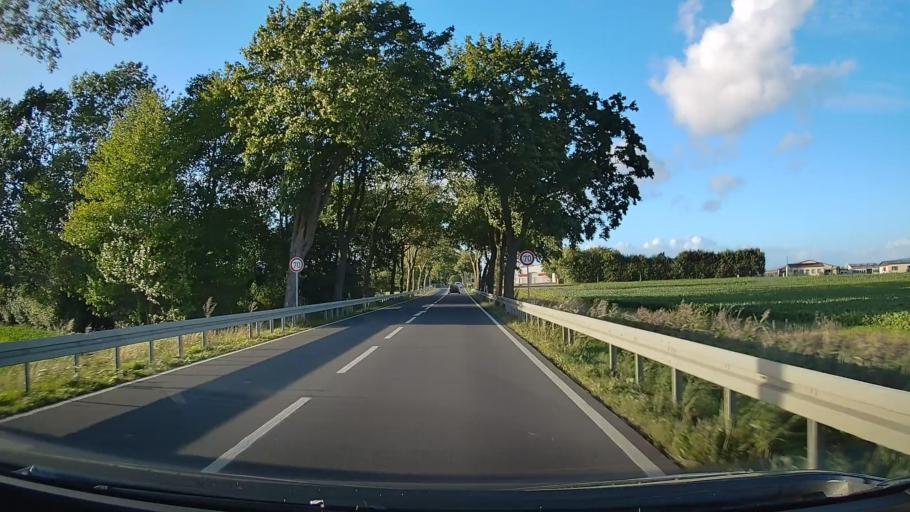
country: DE
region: Mecklenburg-Vorpommern
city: Steinhagen
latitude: 54.2225
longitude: 13.0019
